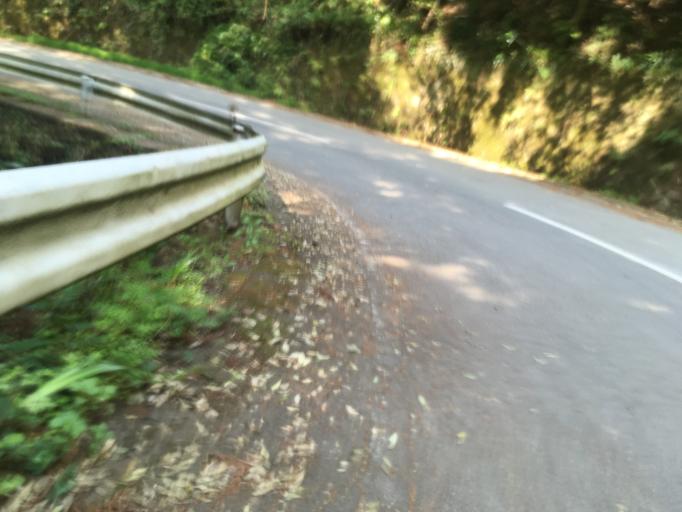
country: JP
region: Kyoto
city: Kameoka
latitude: 35.0875
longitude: 135.6117
